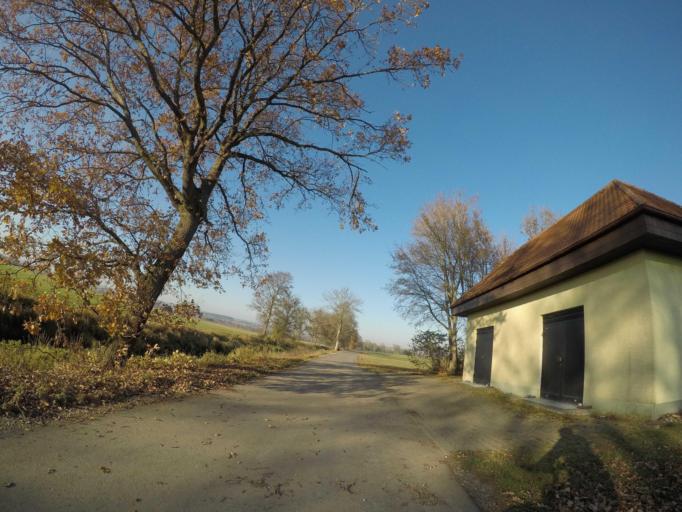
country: DE
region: Baden-Wuerttemberg
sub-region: Tuebingen Region
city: Unterstadion
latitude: 48.2090
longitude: 9.6816
